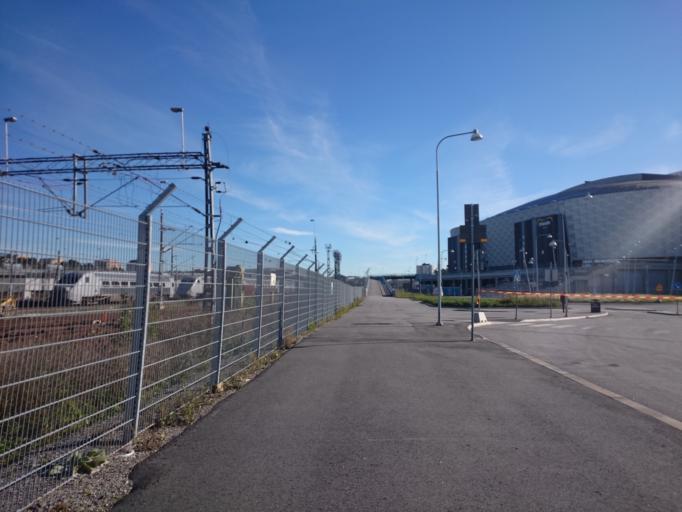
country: SE
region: Stockholm
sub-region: Solna Kommun
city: Rasunda
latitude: 59.3739
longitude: 17.9952
